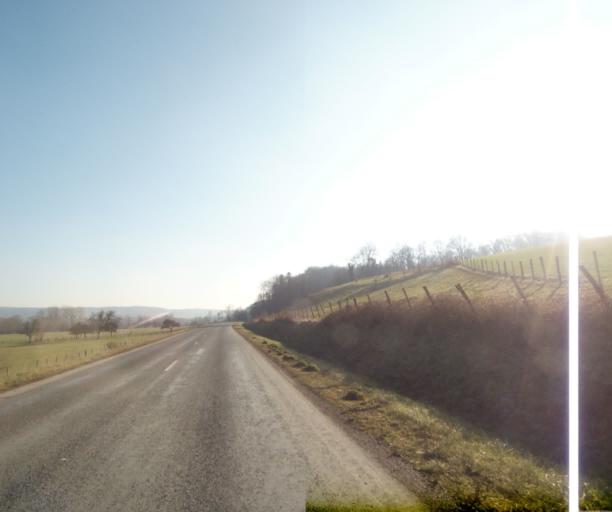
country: FR
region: Champagne-Ardenne
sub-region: Departement de la Haute-Marne
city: Chevillon
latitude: 48.5025
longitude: 5.1169
